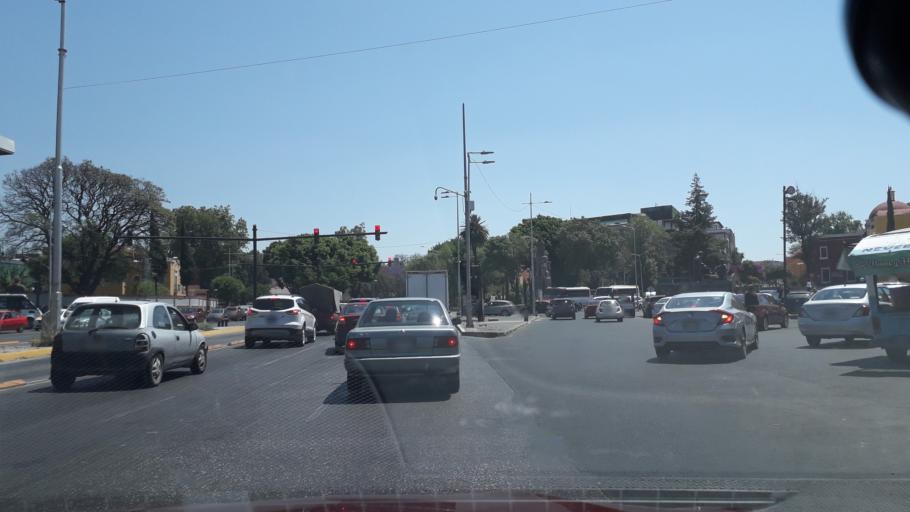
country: MX
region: Puebla
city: Puebla
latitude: 19.0452
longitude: -98.1910
